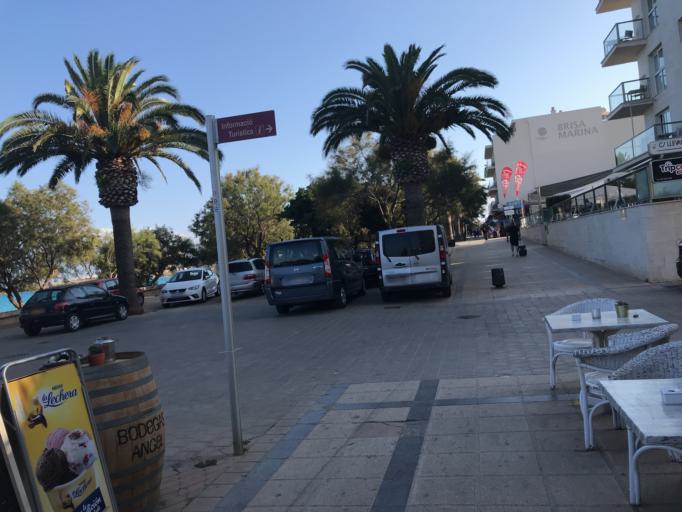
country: ES
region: Balearic Islands
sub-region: Illes Balears
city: Son Servera
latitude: 39.5690
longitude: 3.3741
